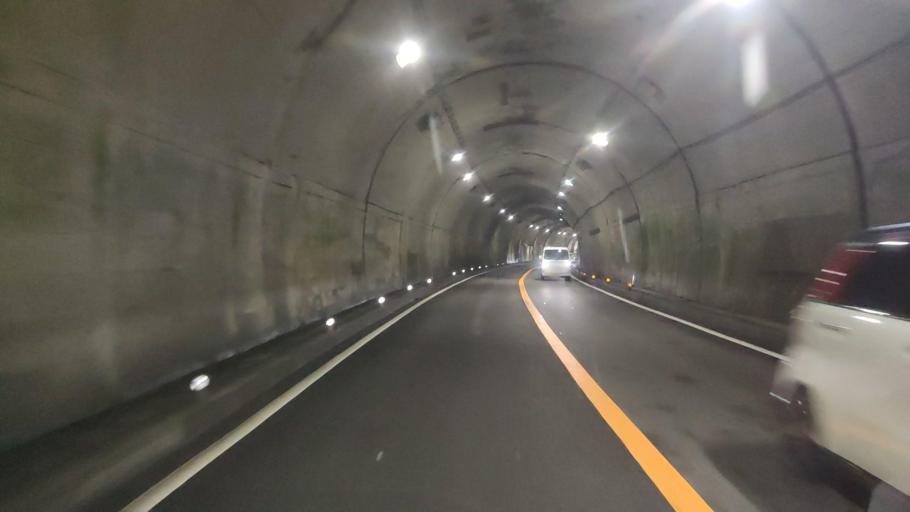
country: JP
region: Wakayama
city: Shingu
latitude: 33.7659
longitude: 135.9073
